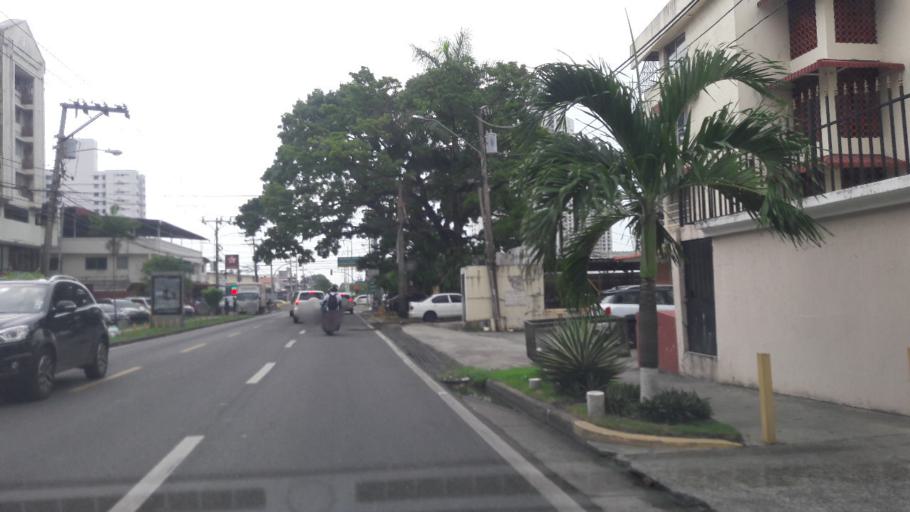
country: PA
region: Panama
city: Panama
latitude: 9.0061
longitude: -79.4995
